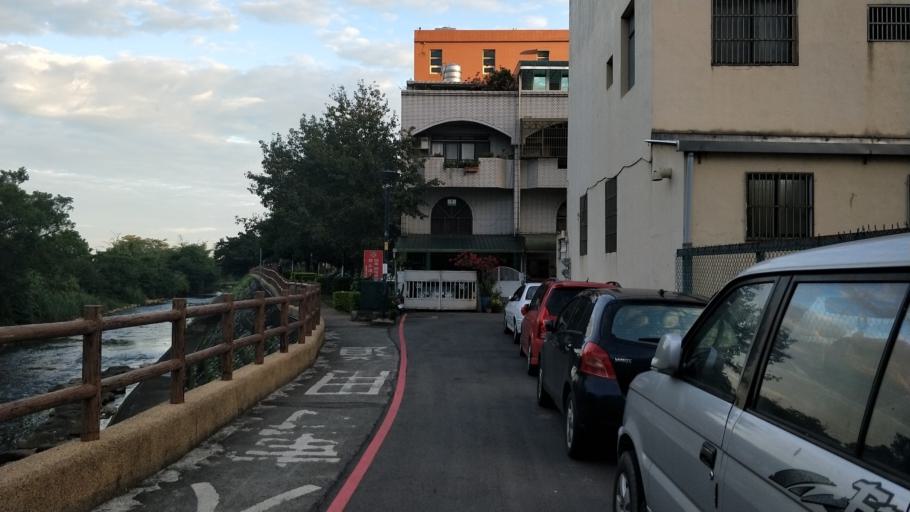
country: TW
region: Taiwan
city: Taoyuan City
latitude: 24.9737
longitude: 121.2337
